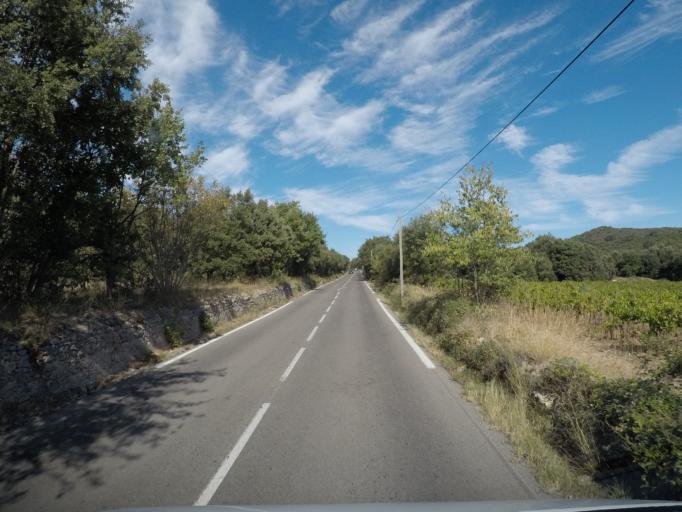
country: FR
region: Languedoc-Roussillon
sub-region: Departement du Gard
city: Sauve
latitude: 43.9797
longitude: 3.9284
